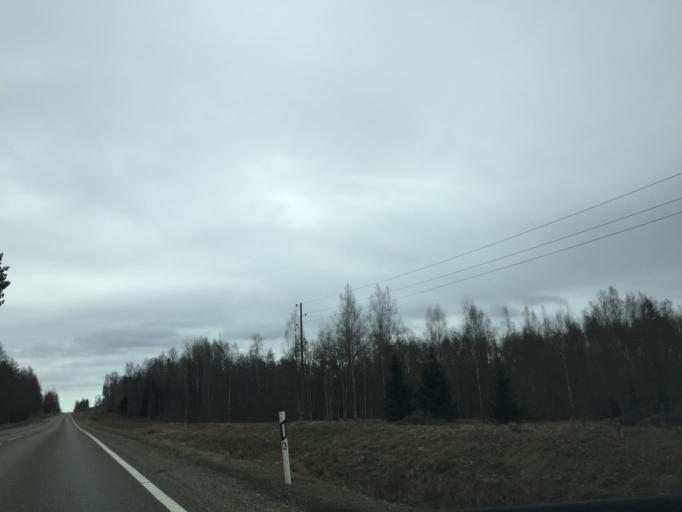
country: LV
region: Kraslavas Rajons
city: Kraslava
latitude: 55.9088
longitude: 27.0960
